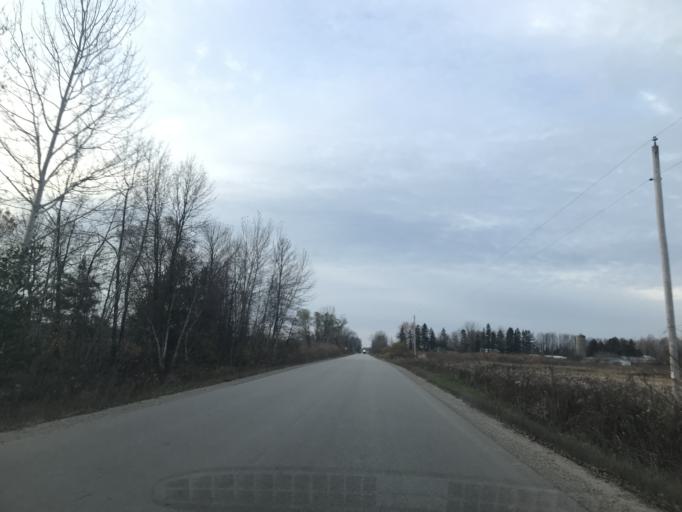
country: US
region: Wisconsin
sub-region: Marinette County
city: Peshtigo
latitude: 45.0926
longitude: -87.7995
